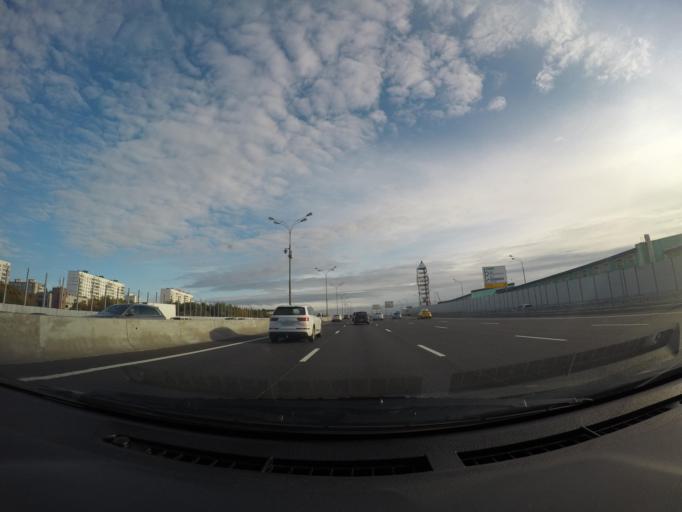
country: RU
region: Moscow
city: Tyoply Stan
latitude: 55.6151
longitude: 37.4873
